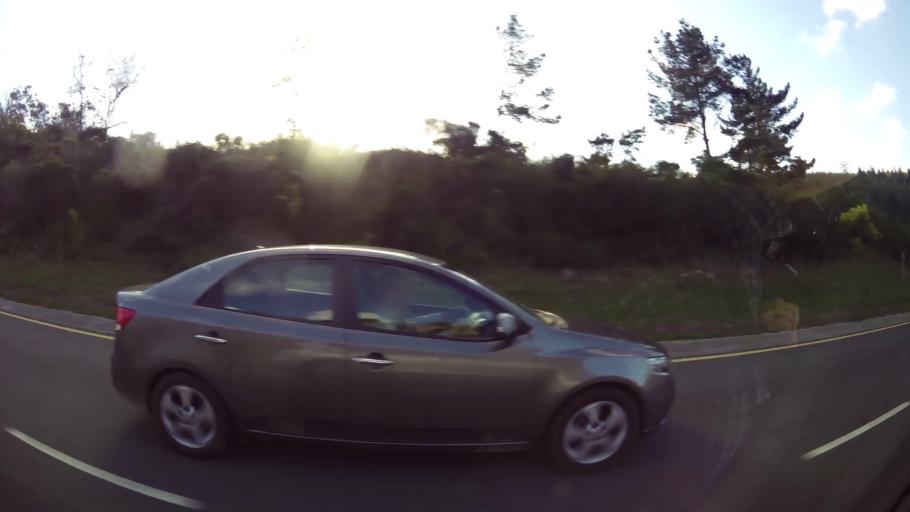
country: ZA
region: Western Cape
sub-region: Eden District Municipality
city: George
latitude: -33.9873
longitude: 22.5412
